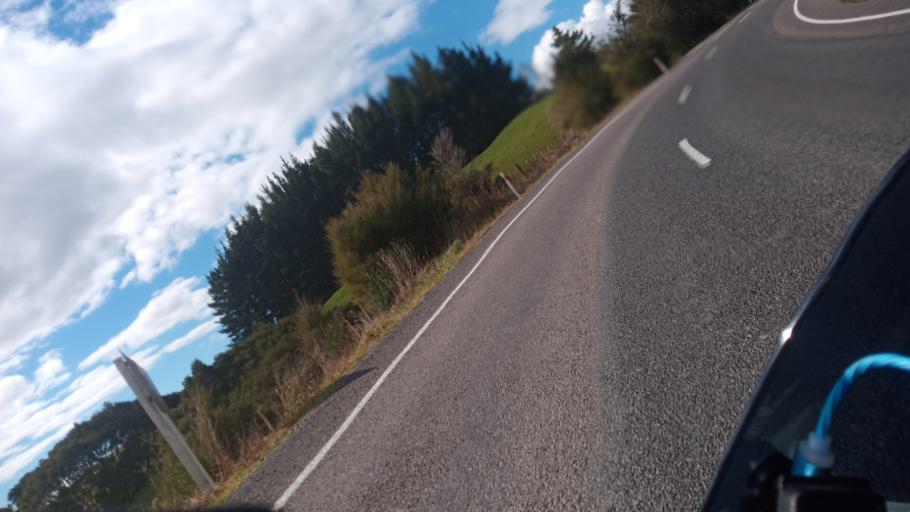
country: NZ
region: Gisborne
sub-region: Gisborne District
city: Gisborne
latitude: -37.9034
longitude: 178.2784
